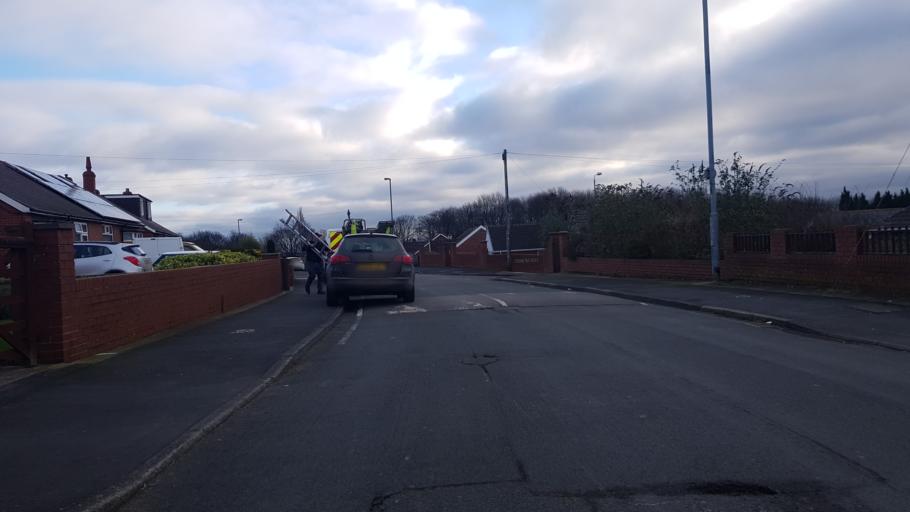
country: GB
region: England
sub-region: City and Borough of Wakefield
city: Pontefract
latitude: 53.7178
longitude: -1.3290
